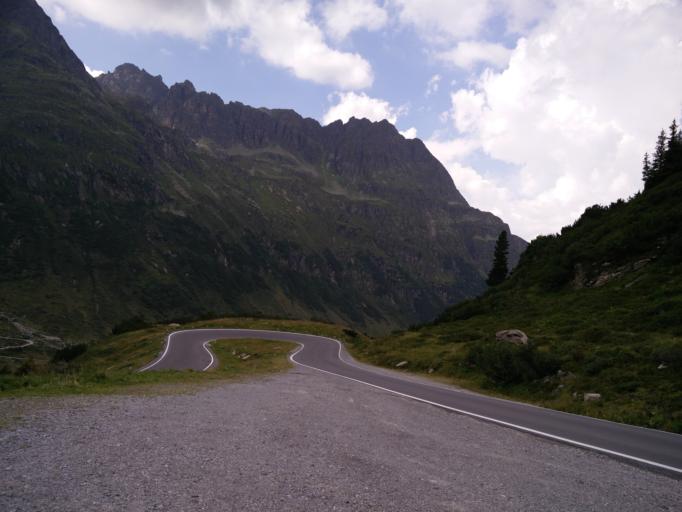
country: AT
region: Vorarlberg
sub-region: Politischer Bezirk Bludenz
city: Gaschurn
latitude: 46.9218
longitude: 10.0580
